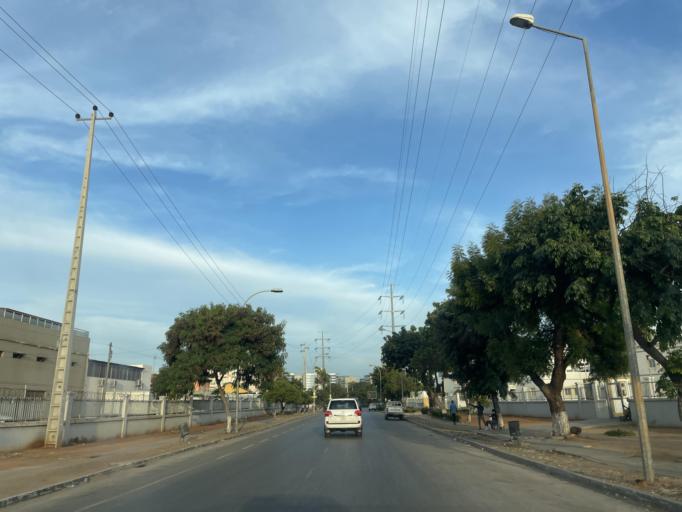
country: AO
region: Luanda
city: Luanda
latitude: -8.9238
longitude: 13.1822
